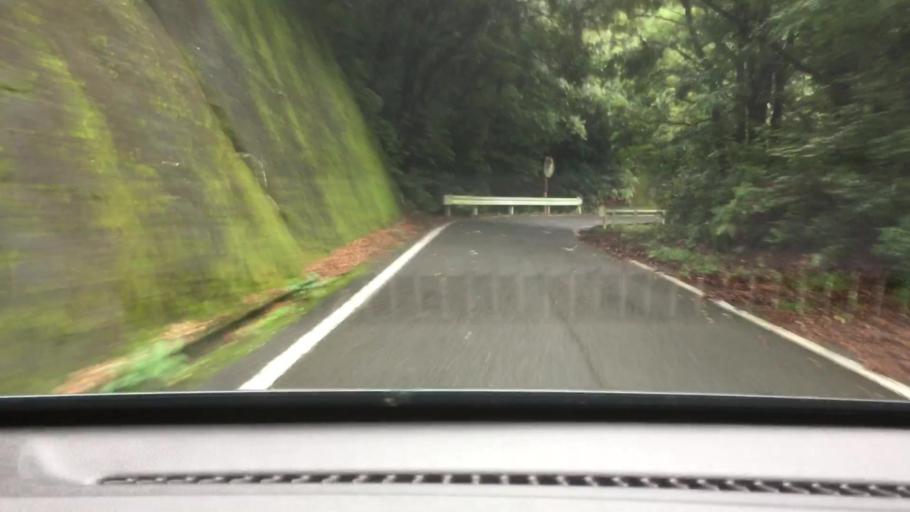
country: JP
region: Nagasaki
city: Togitsu
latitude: 32.9211
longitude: 129.7269
